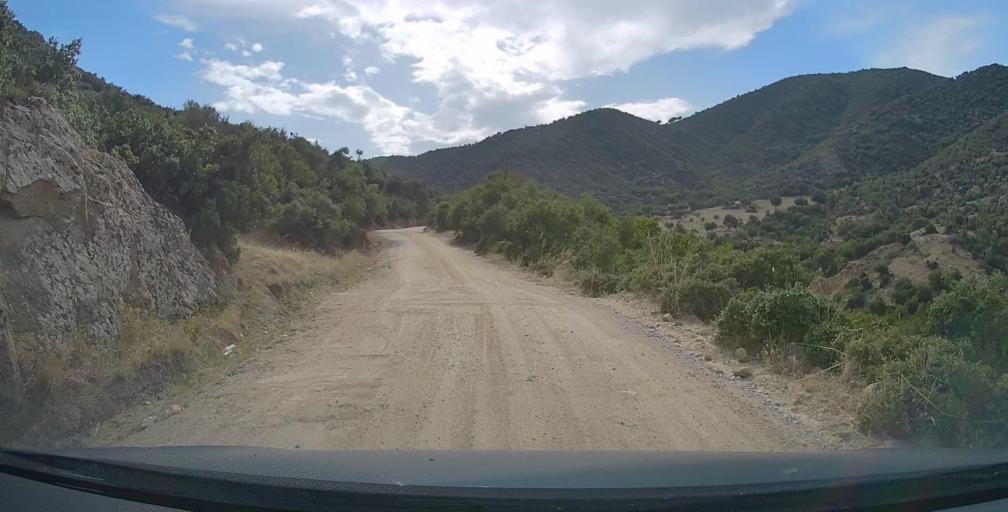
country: GR
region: Central Macedonia
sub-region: Nomos Chalkidikis
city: Sykia
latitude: 40.0201
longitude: 23.9406
